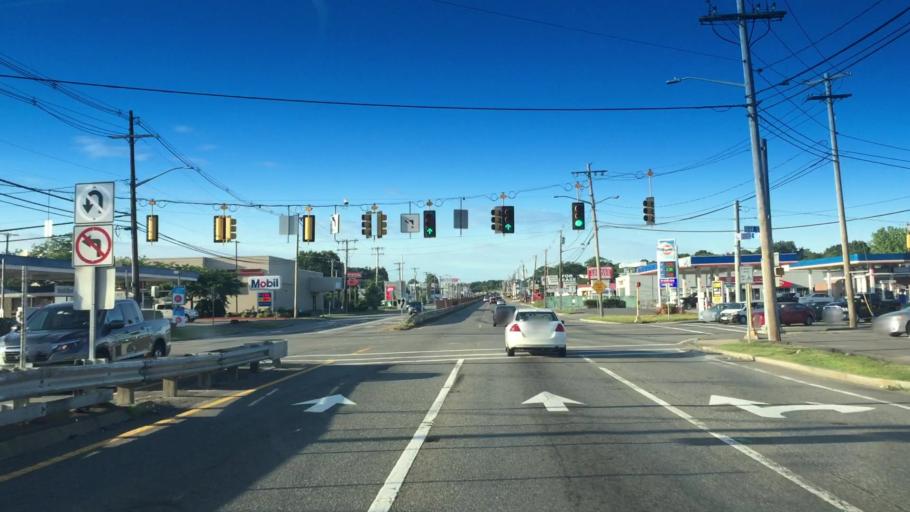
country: US
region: Massachusetts
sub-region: Norfolk County
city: Norwood
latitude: 42.1785
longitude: -71.1908
